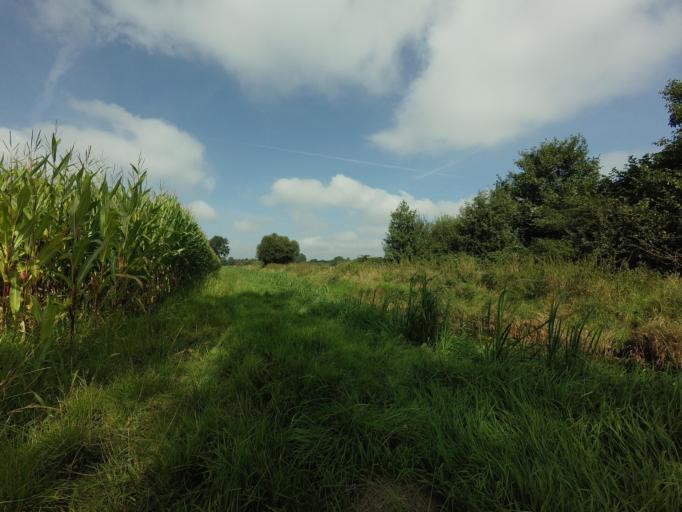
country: NL
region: Drenthe
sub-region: Gemeente Tynaarlo
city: Vries
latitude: 53.1115
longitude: 6.5502
